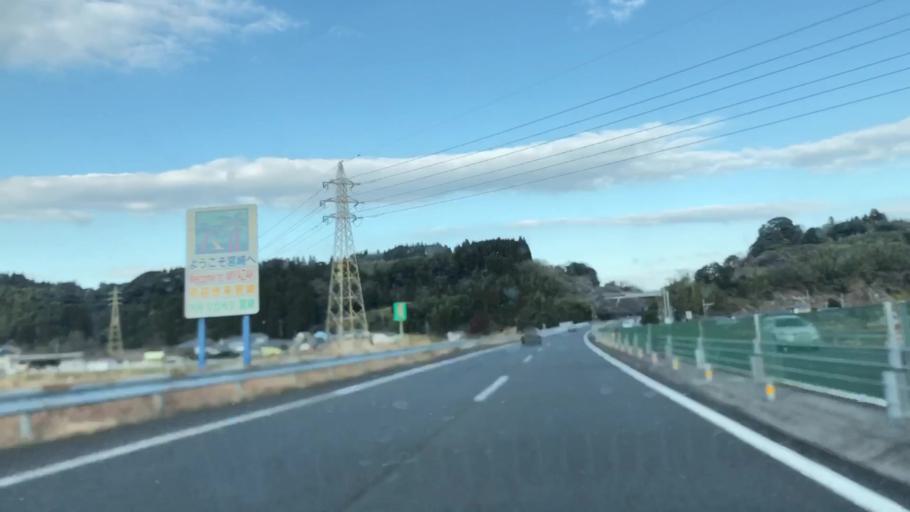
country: JP
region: Miyazaki
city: Miyazaki-shi
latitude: 31.8619
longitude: 131.3805
